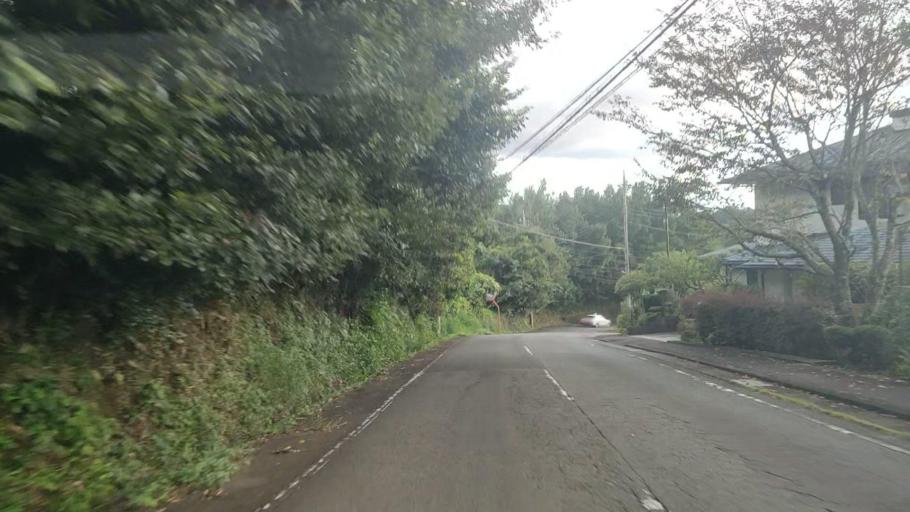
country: JP
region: Shizuoka
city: Mishima
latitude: 35.1152
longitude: 138.9770
